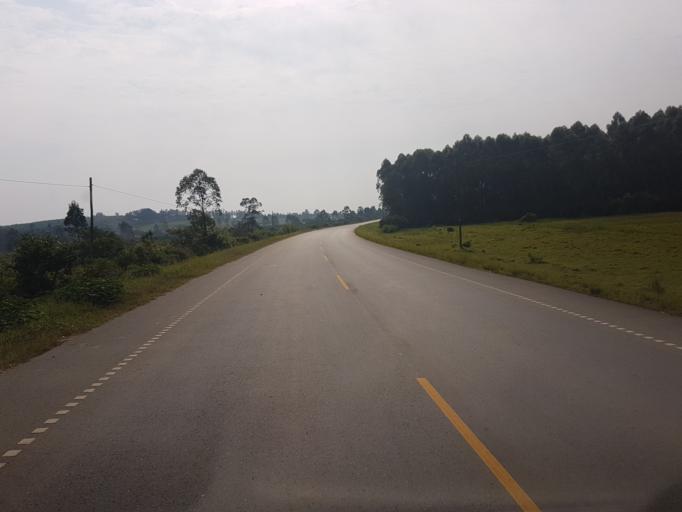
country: UG
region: Western Region
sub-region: Sheema District
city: Kibingo
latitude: -0.6488
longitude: 30.4871
